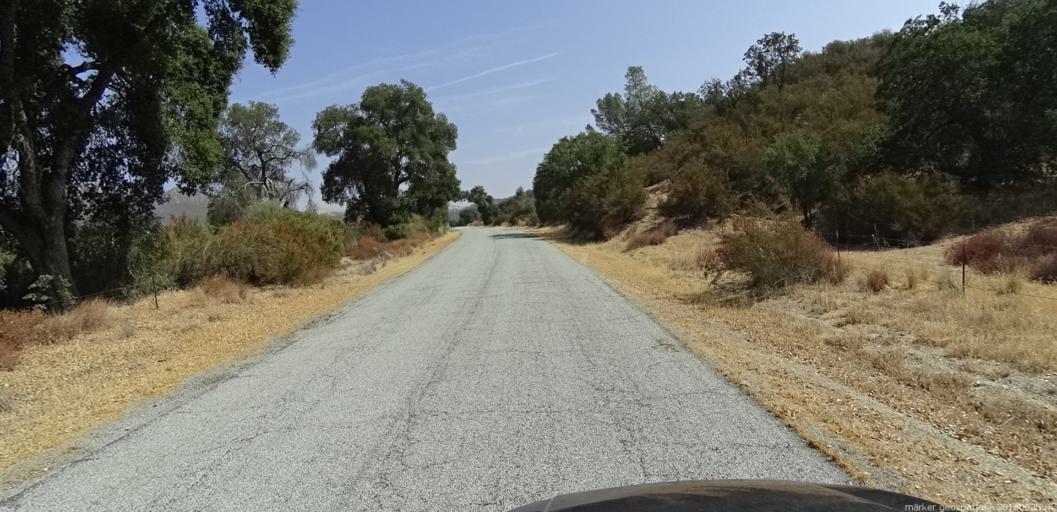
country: US
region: California
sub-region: San Luis Obispo County
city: San Miguel
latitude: 35.8944
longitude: -120.5550
